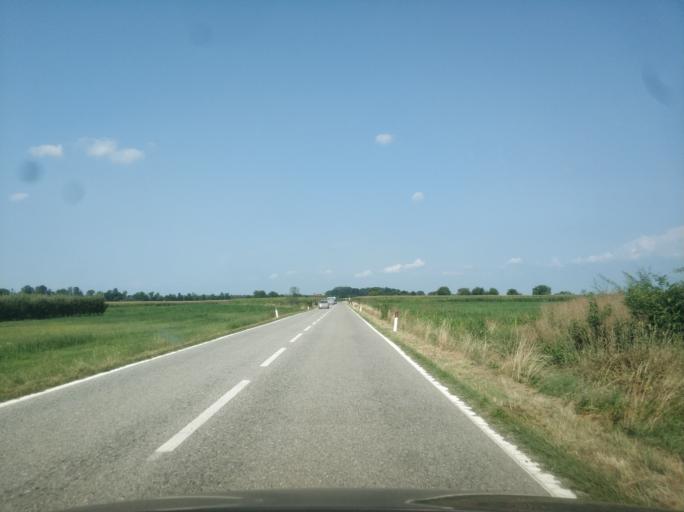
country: IT
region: Piedmont
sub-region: Provincia di Cuneo
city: Caraglio
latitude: 44.4383
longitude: 7.4489
